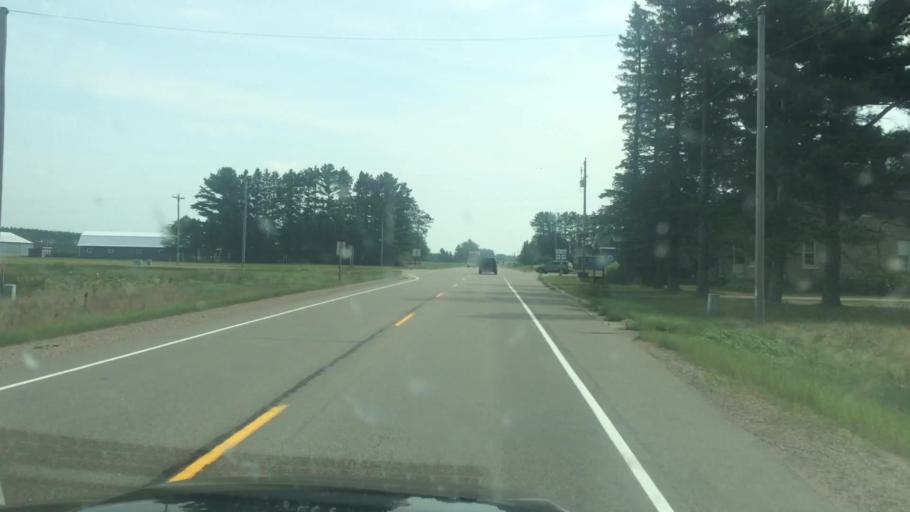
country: US
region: Wisconsin
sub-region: Langlade County
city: Antigo
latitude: 45.1400
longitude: -89.2104
